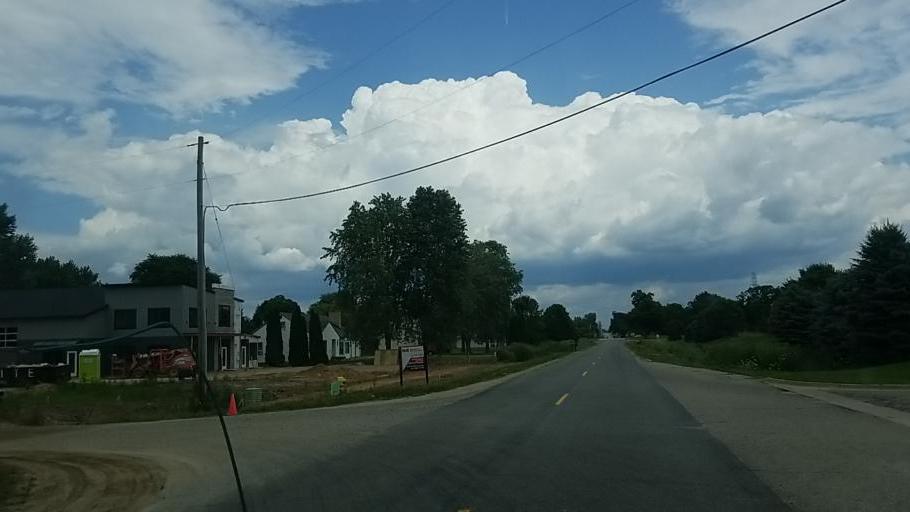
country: US
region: Michigan
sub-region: Kent County
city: Walker
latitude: 43.0161
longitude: -85.7921
